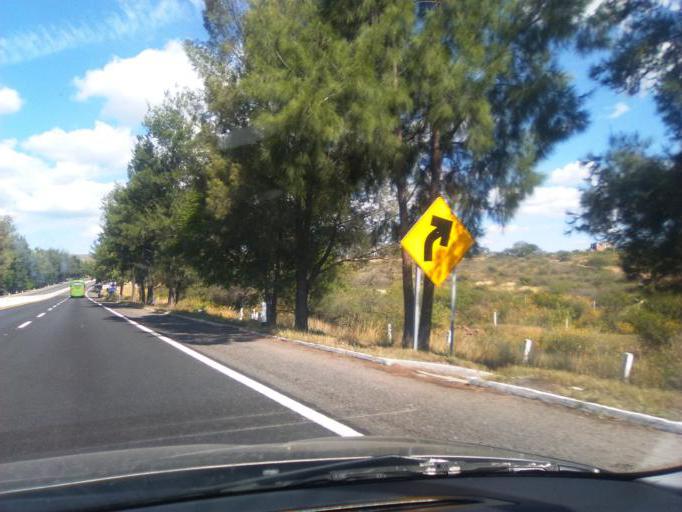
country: MX
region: Guanajuato
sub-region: Guanajuato
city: San Jose de Cervera
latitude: 20.9728
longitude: -101.3045
